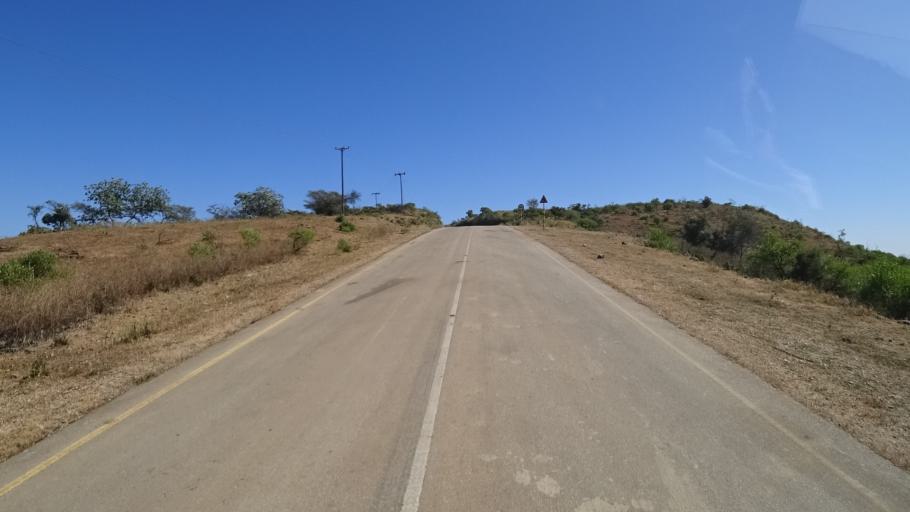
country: YE
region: Al Mahrah
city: Hawf
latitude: 16.7438
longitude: 53.3603
